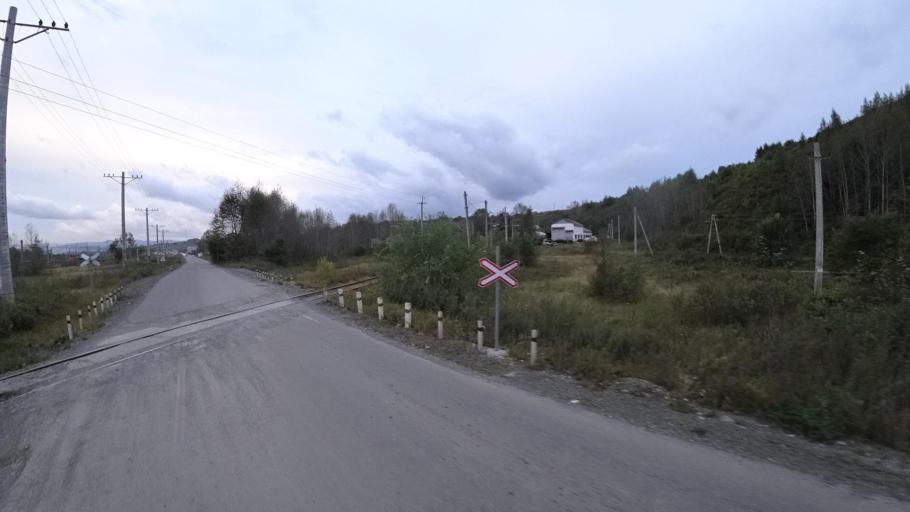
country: RU
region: Jewish Autonomous Oblast
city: Izvestkovyy
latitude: 48.9887
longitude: 131.5427
